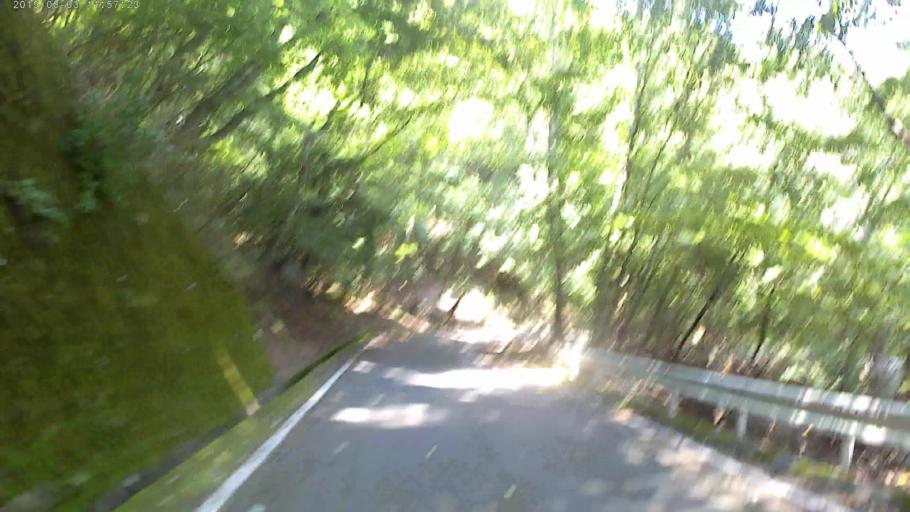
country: JP
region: Yamanashi
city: Enzan
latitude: 35.6119
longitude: 138.7825
